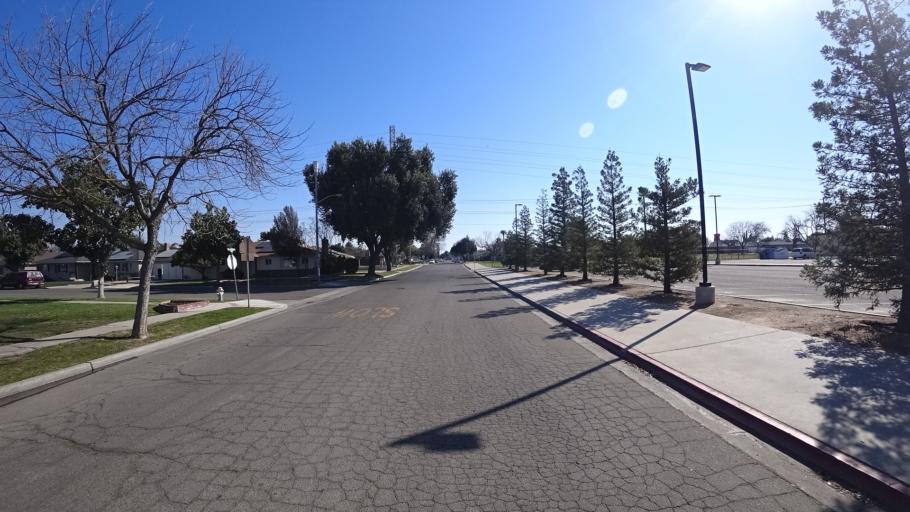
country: US
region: California
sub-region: Fresno County
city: Clovis
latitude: 36.8267
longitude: -119.7689
